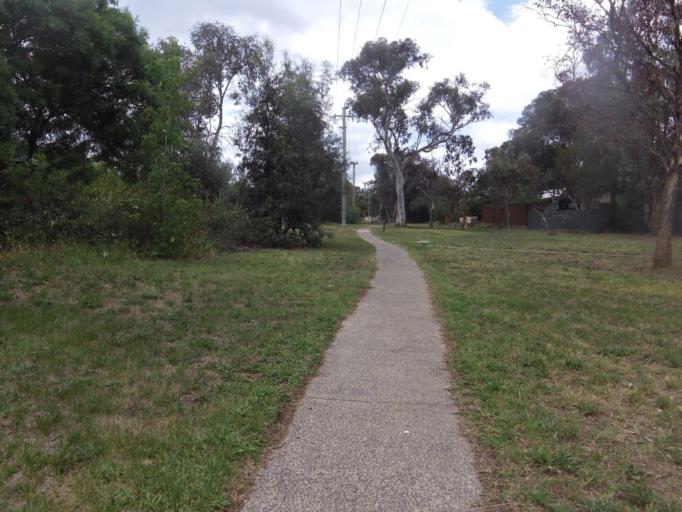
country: AU
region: Australian Capital Territory
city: Macarthur
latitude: -35.4069
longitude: 149.1281
